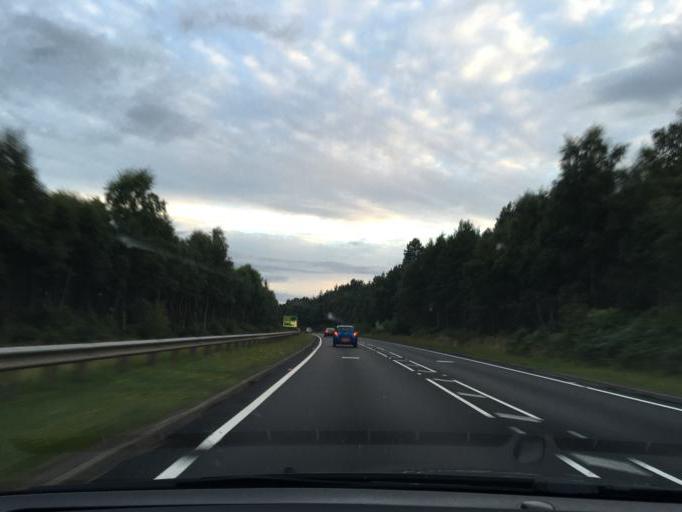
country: GB
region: Scotland
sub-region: Highland
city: Aviemore
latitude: 57.2303
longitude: -3.8155
